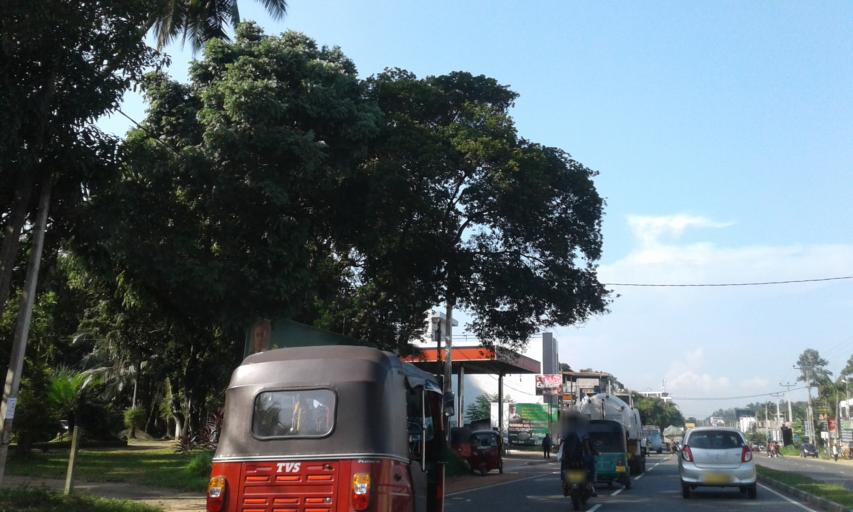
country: LK
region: Western
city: Gampaha
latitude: 7.0278
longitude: 79.9815
